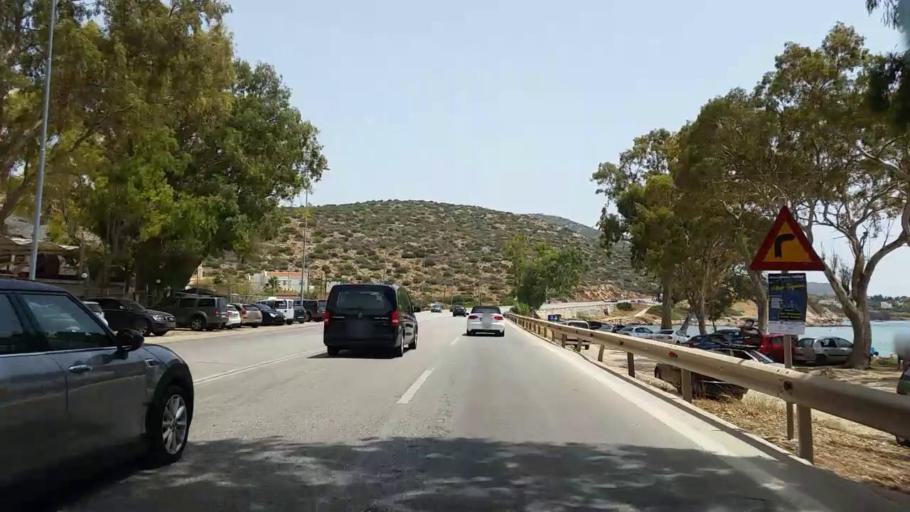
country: GR
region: Attica
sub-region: Nomarchia Anatolikis Attikis
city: Saronida
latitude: 37.7754
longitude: 23.9003
